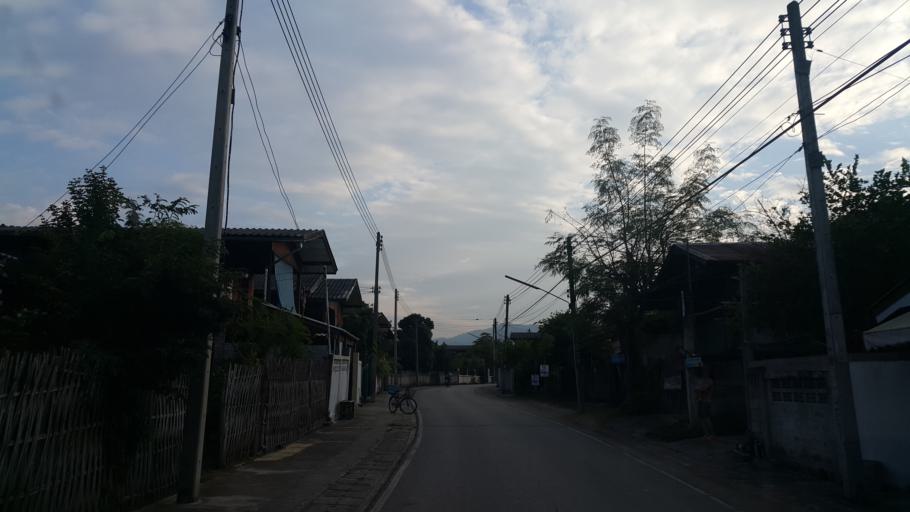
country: TH
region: Lampang
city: Sop Prap
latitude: 17.8687
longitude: 99.3311
